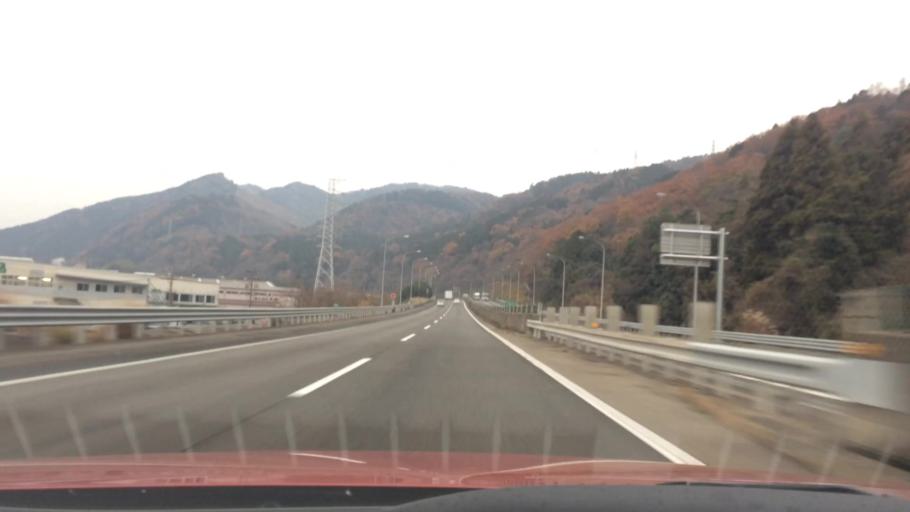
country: JP
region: Gifu
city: Tarui
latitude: 35.3289
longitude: 136.5336
